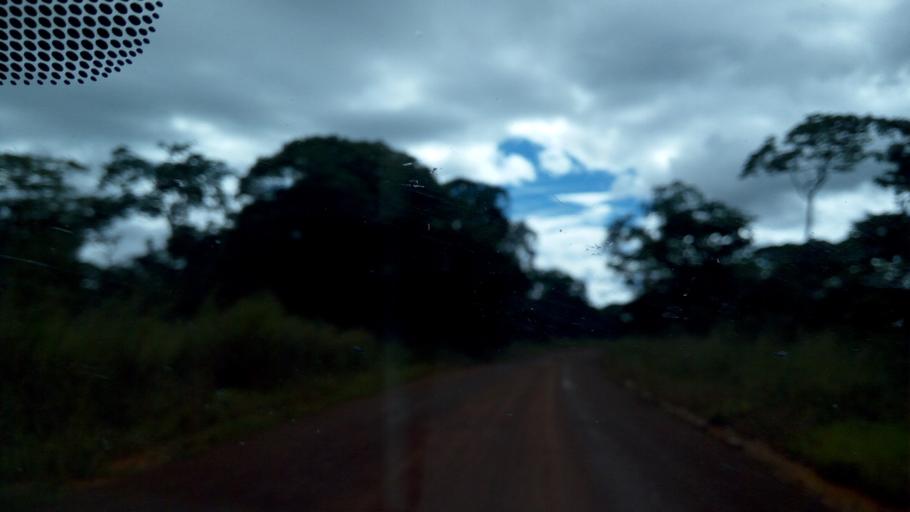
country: ZM
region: Luapula
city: Mwense
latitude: -10.7108
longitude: 28.1818
